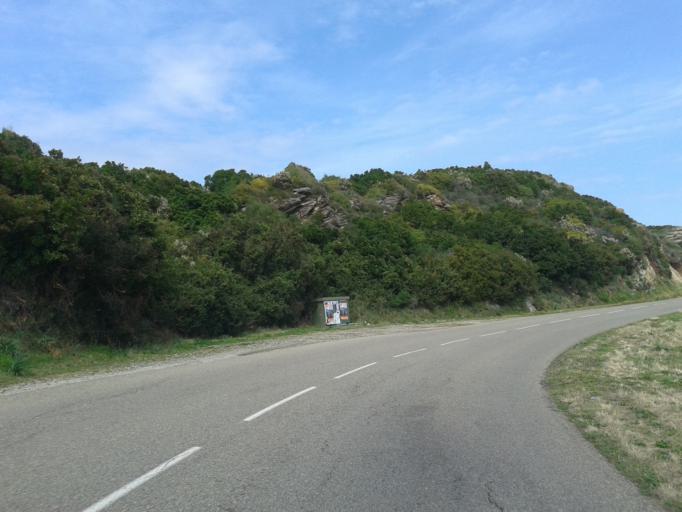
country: FR
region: Corsica
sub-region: Departement de la Haute-Corse
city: Brando
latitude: 42.8441
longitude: 9.4822
